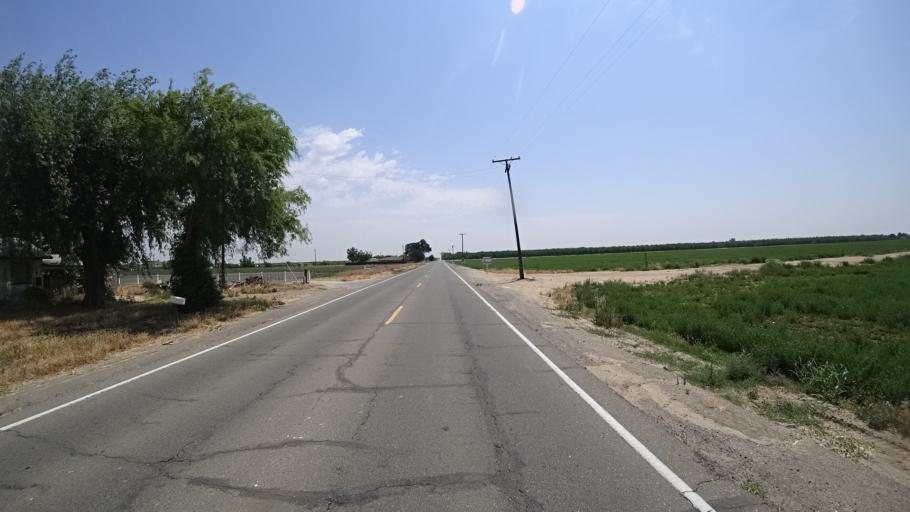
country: US
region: California
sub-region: Kings County
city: Lemoore
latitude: 36.3281
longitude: -119.7768
